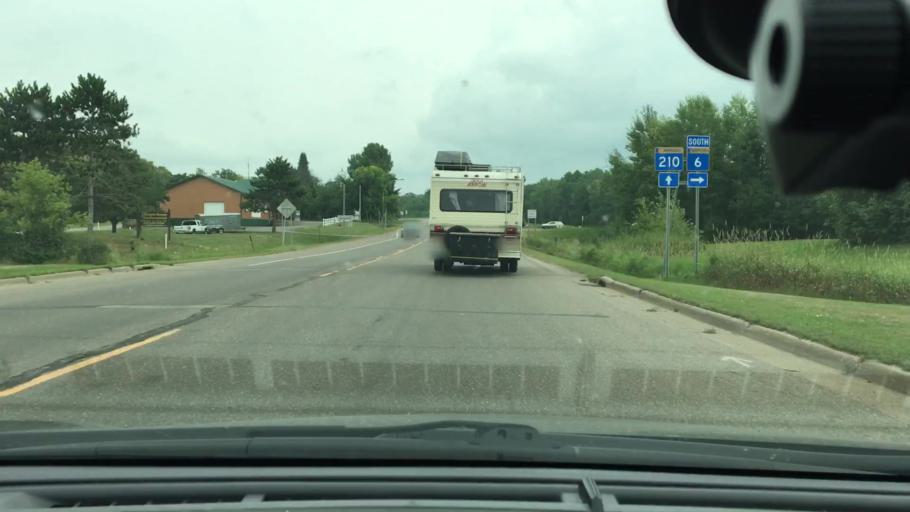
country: US
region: Minnesota
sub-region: Crow Wing County
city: Crosby
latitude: 46.4749
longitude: -93.8948
